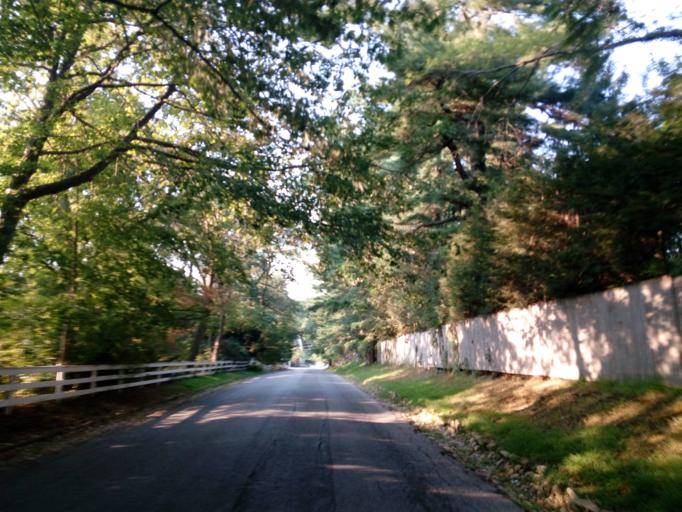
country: US
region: New York
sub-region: Nassau County
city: Lattingtown
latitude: 40.8871
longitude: -73.6079
